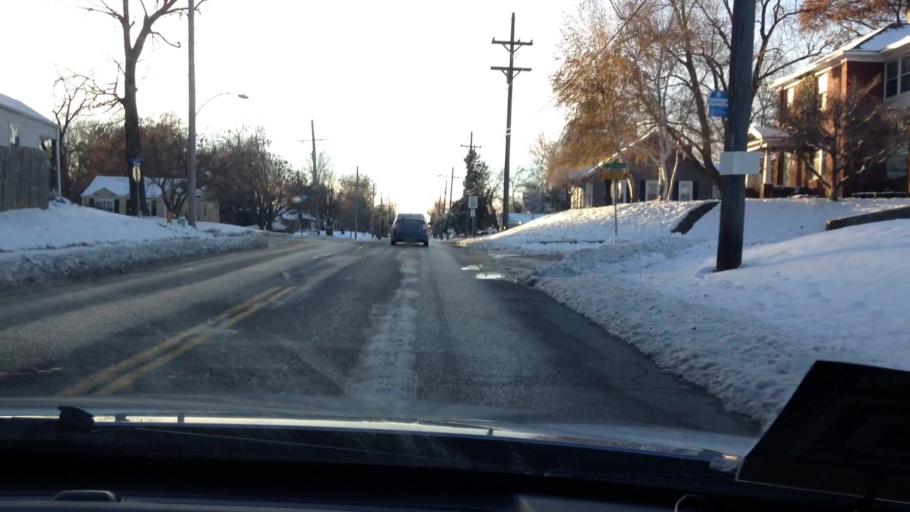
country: US
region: Kansas
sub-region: Johnson County
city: Westwood
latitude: 39.0441
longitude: -94.6248
